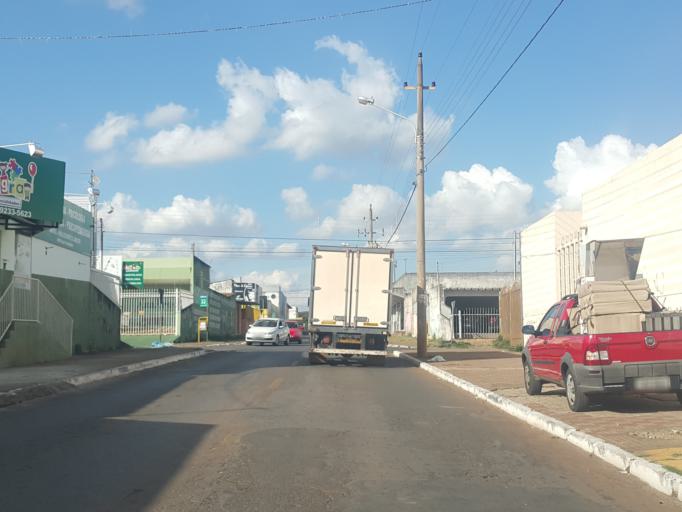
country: BR
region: Federal District
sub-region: Brasilia
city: Brasilia
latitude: -15.8230
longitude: -48.0604
